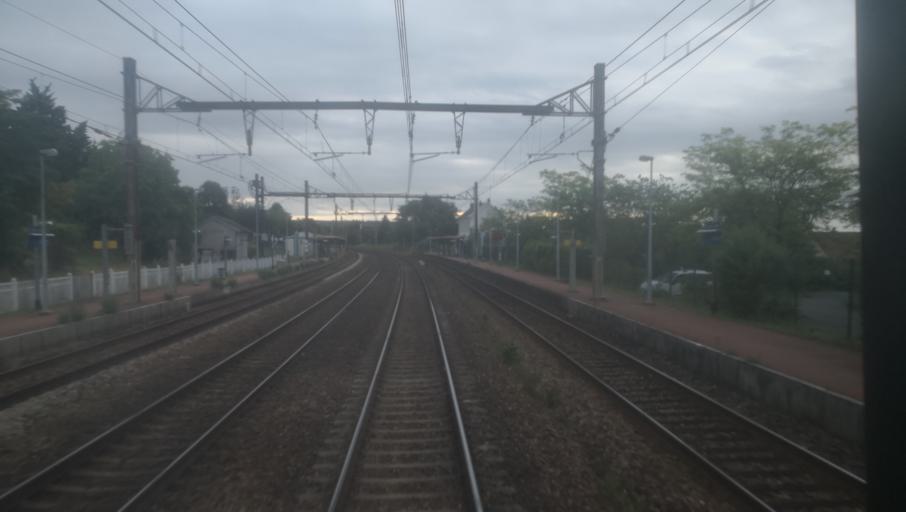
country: FR
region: Ile-de-France
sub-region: Departement de l'Essonne
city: Janville-sur-Juine
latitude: 48.5198
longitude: 2.2535
